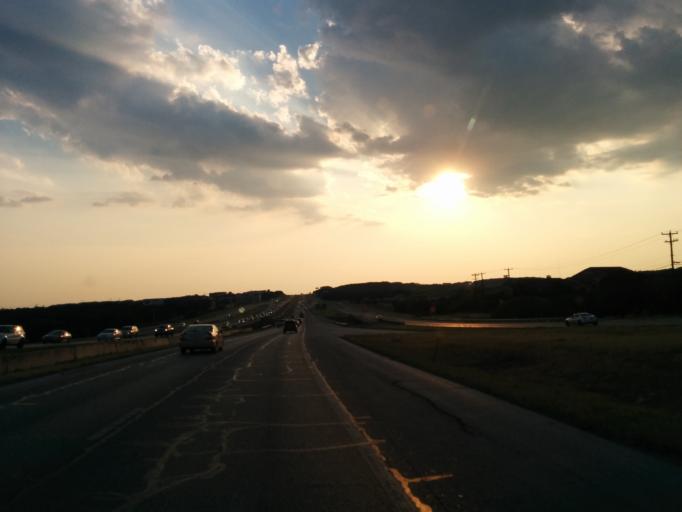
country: US
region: Texas
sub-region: Bexar County
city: Shavano Park
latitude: 29.6025
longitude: -98.5375
